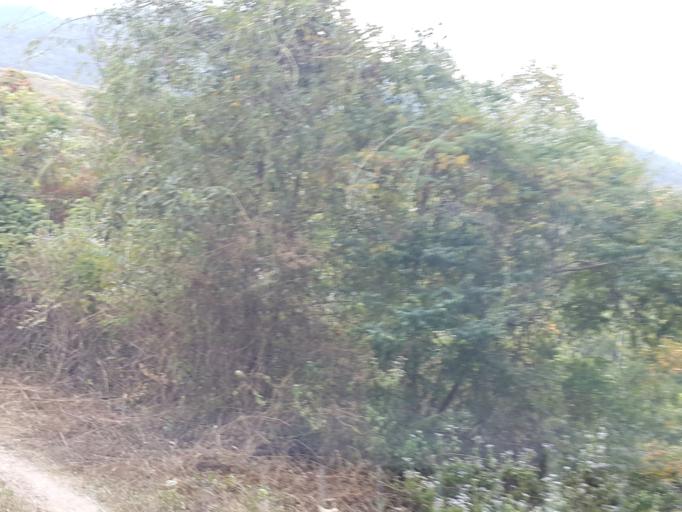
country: TH
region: Chiang Mai
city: Om Koi
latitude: 17.7992
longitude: 98.3341
